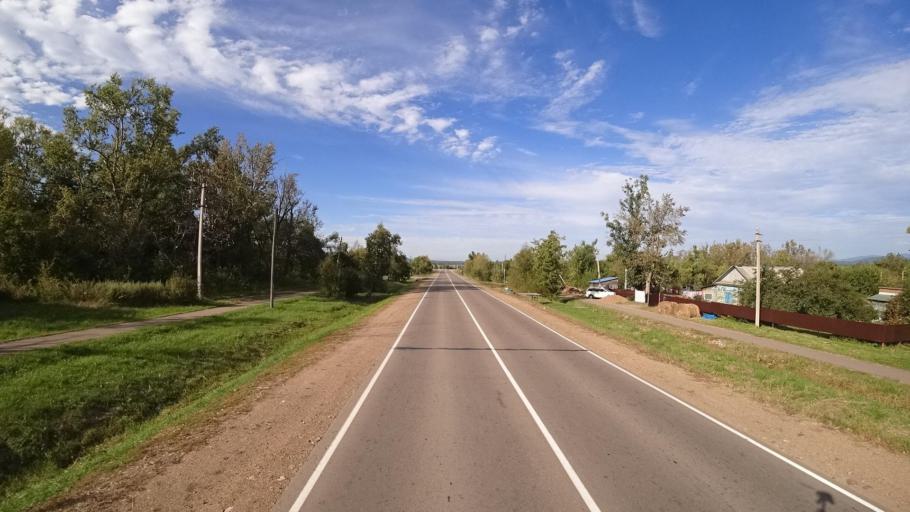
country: RU
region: Primorskiy
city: Dostoyevka
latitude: 44.3030
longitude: 133.4495
